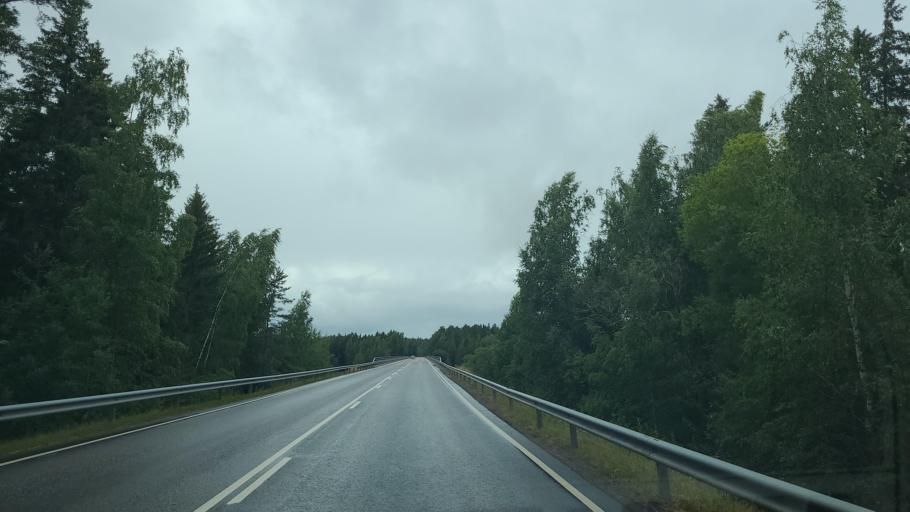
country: FI
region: Varsinais-Suomi
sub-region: Aboland-Turunmaa
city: Kimito
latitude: 60.2280
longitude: 22.6131
